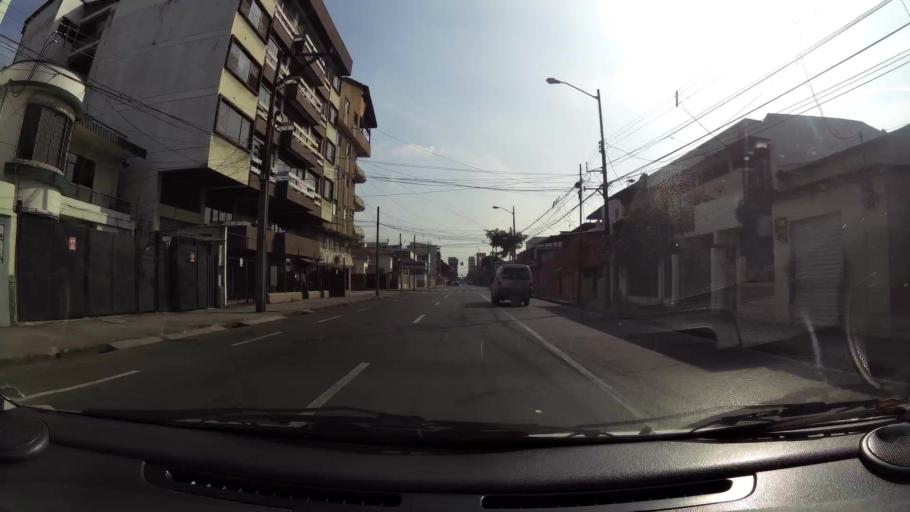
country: EC
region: Guayas
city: Guayaquil
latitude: -2.1933
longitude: -79.8974
